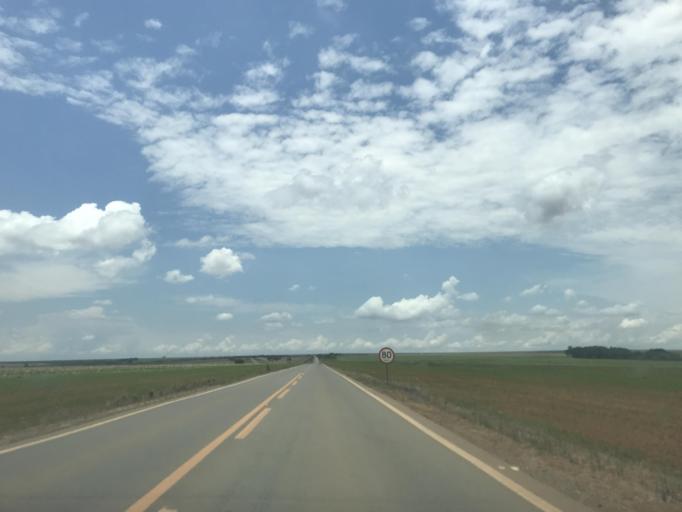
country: BR
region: Goias
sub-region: Luziania
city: Luziania
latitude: -16.4989
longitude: -48.2060
